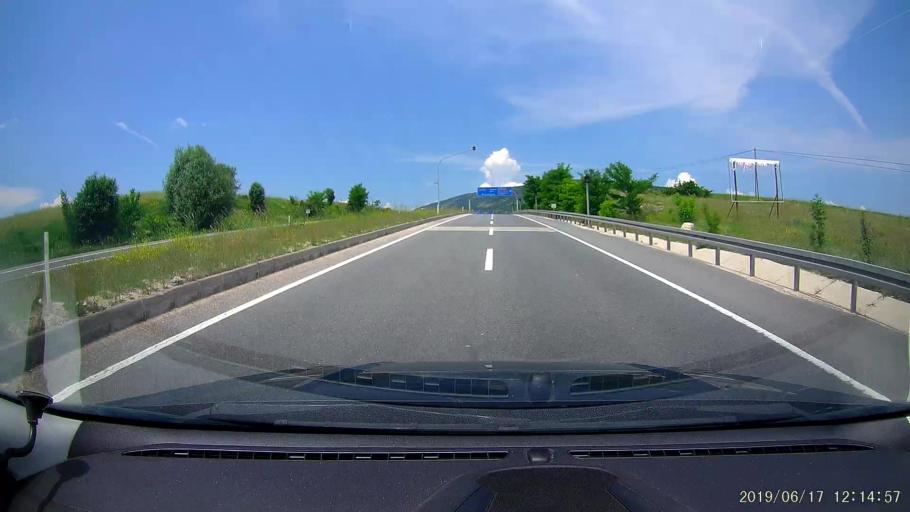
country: TR
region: Karabuk
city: Gozyeri
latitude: 40.8700
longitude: 32.5870
